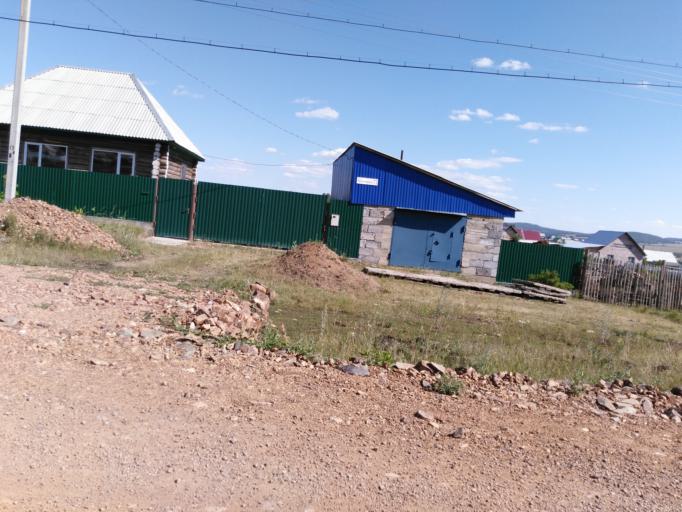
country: RU
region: Bashkortostan
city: Uchaly
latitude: 54.2933
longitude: 59.3621
